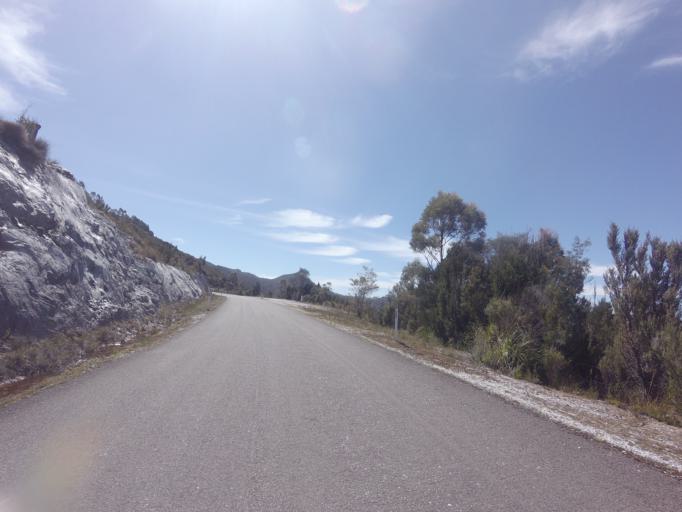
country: AU
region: Tasmania
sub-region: West Coast
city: Queenstown
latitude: -42.7388
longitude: 145.9820
